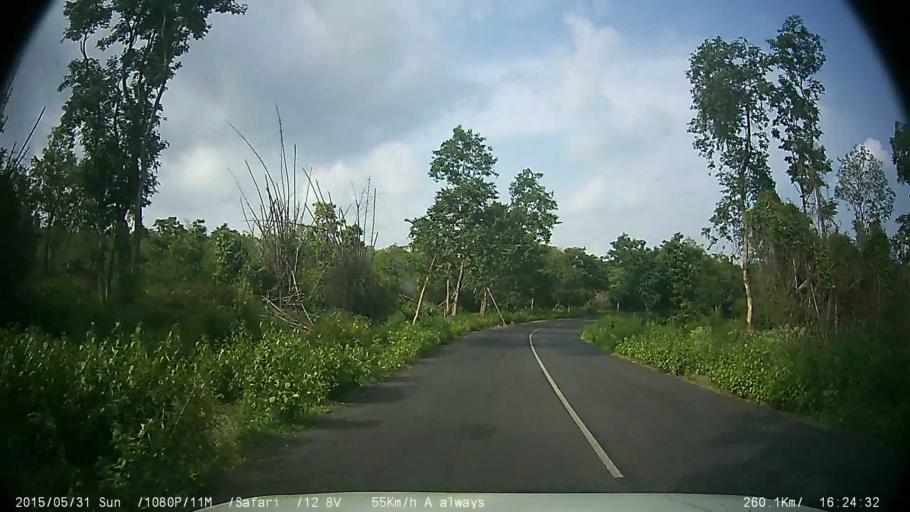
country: IN
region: Karnataka
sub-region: Chamrajnagar
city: Gundlupet
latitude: 11.7646
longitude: 76.5219
